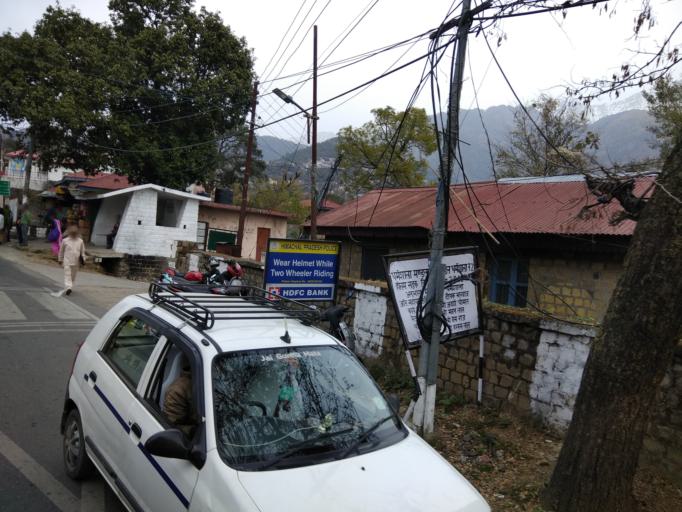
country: IN
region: Himachal Pradesh
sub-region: Kangra
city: Dharmsala
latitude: 32.2102
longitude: 76.3220
